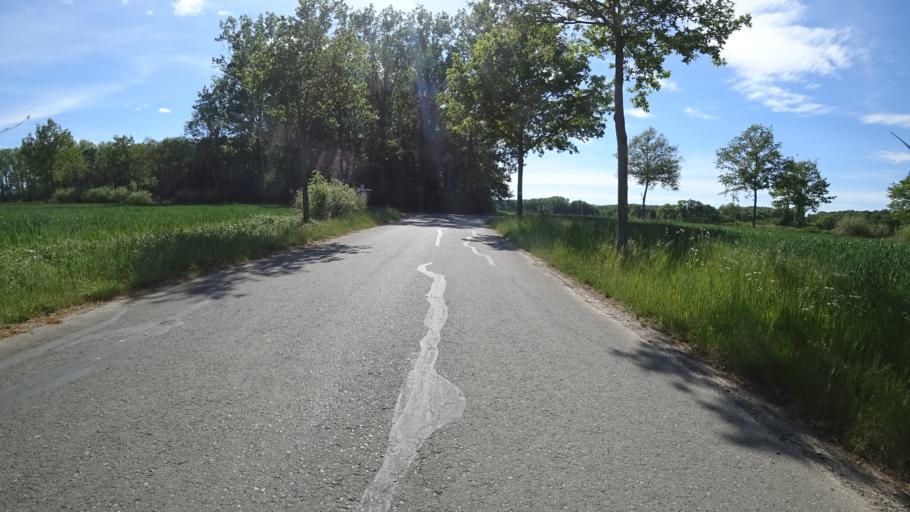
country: DE
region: North Rhine-Westphalia
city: Oelde
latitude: 51.8186
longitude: 8.2225
